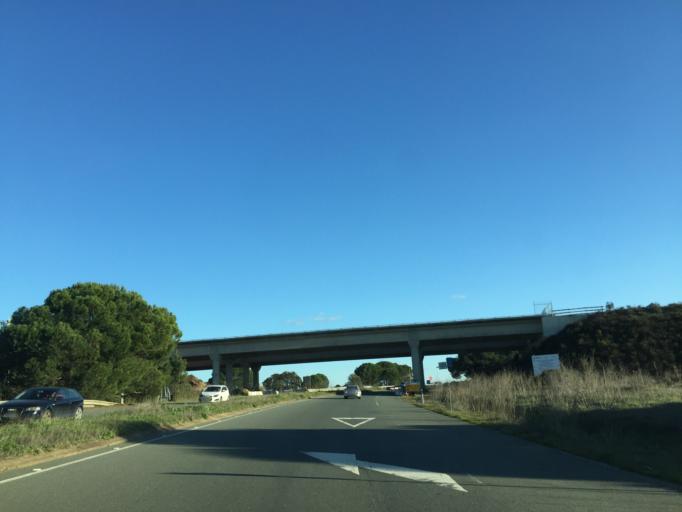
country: PT
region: Setubal
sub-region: Grandola
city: Grandola
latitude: 38.1176
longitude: -8.4208
